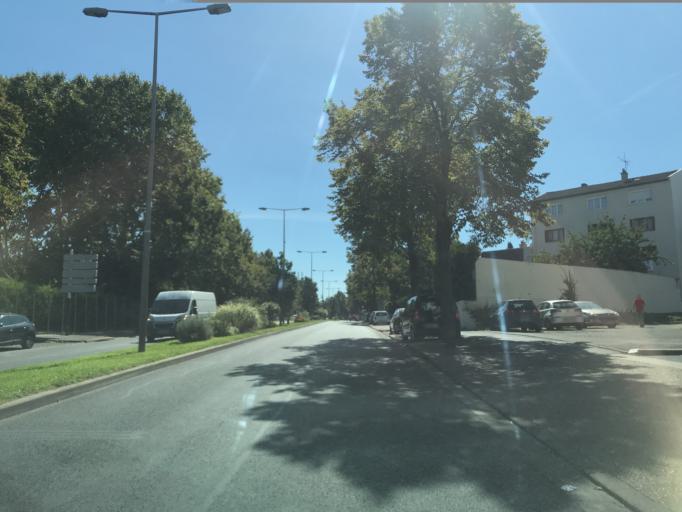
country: FR
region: Ile-de-France
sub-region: Departement de Seine-Saint-Denis
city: Bobigny
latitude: 48.9034
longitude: 2.4400
